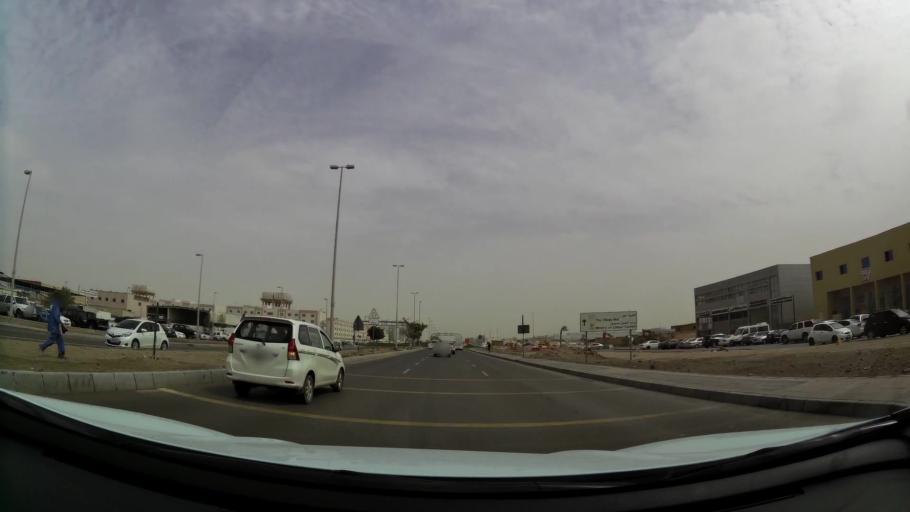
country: AE
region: Abu Dhabi
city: Abu Dhabi
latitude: 24.3598
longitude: 54.5149
